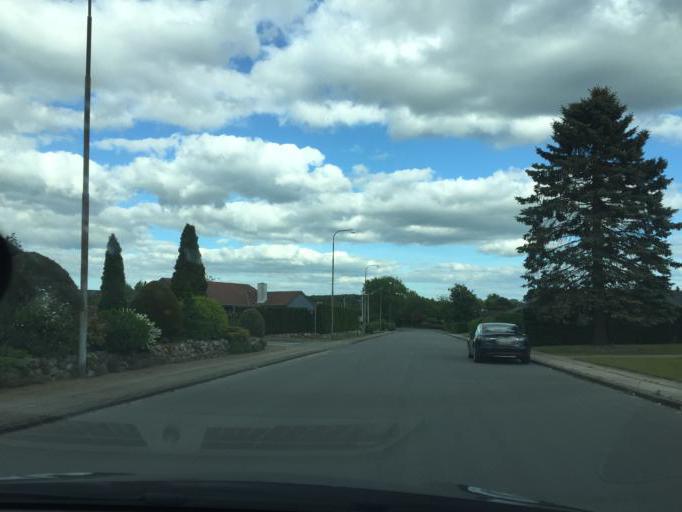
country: DK
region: South Denmark
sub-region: Odense Kommune
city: Bellinge
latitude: 55.3487
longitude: 10.3419
